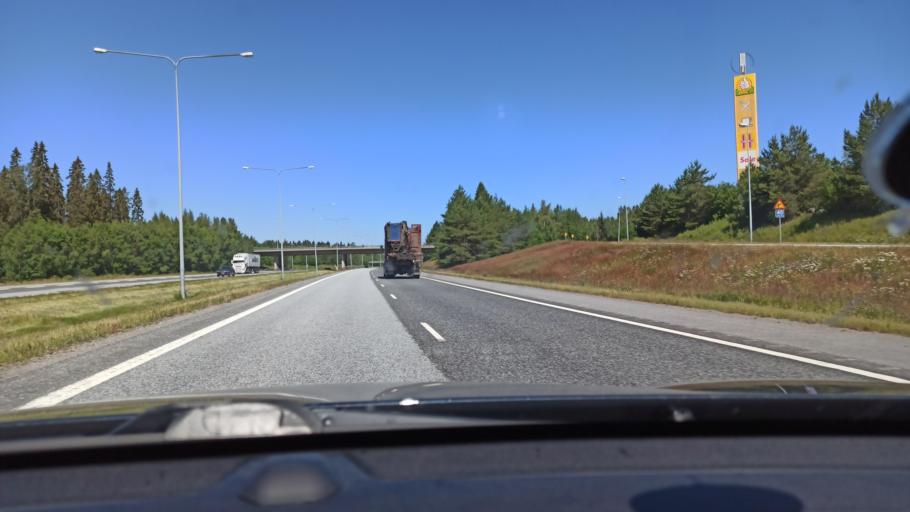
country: FI
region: Ostrobothnia
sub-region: Vaasa
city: Ristinummi
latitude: 63.0522
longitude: 21.7159
